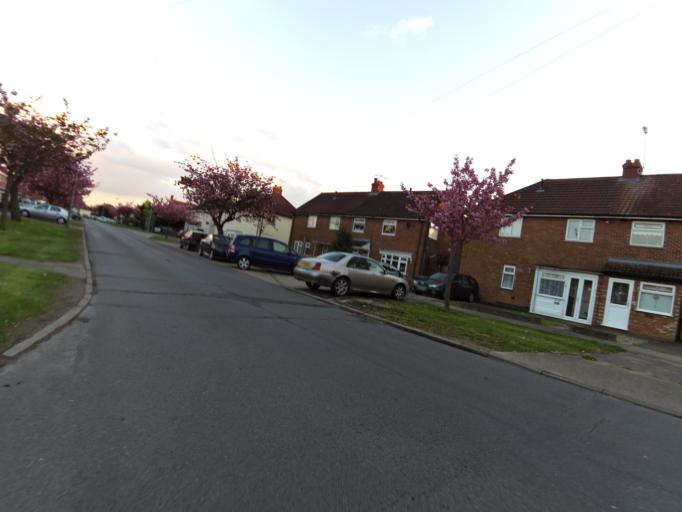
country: GB
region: England
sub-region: Suffolk
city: Ipswich
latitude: 52.0698
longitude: 1.1911
